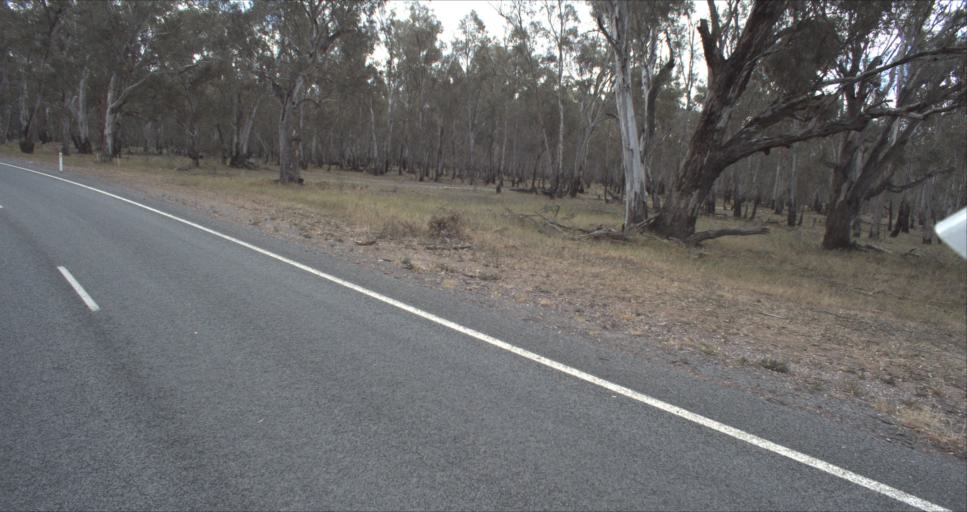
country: AU
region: New South Wales
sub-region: Leeton
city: Leeton
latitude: -34.6410
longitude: 146.3597
